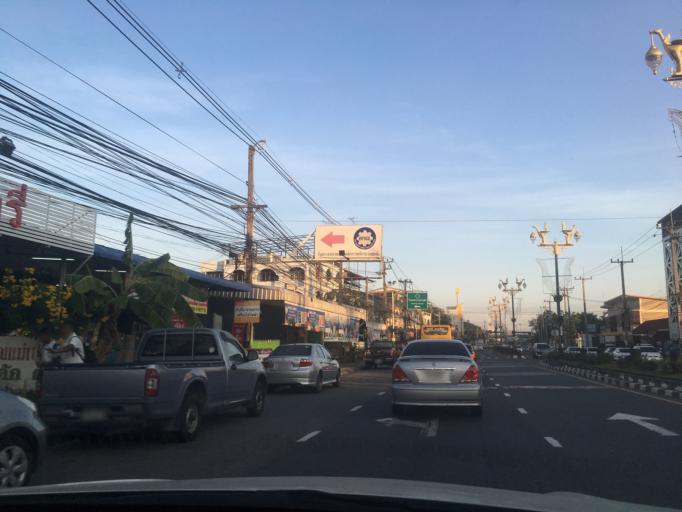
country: TH
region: Chon Buri
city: Ban Bueng
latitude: 13.3149
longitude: 101.1083
